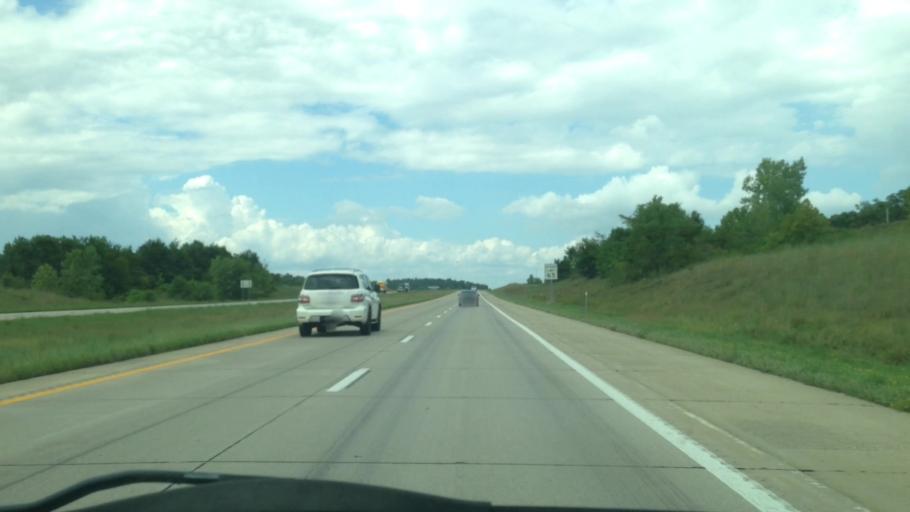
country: US
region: Missouri
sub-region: Pike County
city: Bowling Green
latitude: 39.4101
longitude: -91.2479
